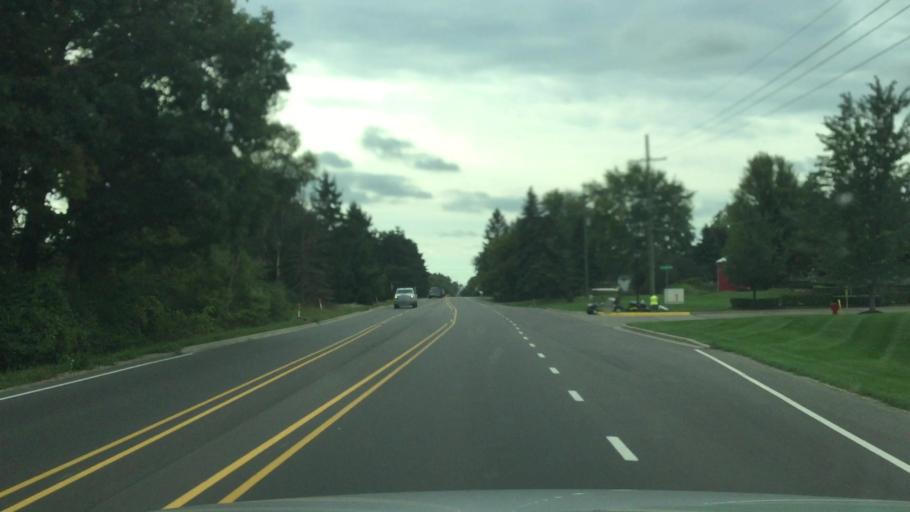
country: US
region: Michigan
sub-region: Livingston County
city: Howell
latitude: 42.6068
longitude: -83.8748
